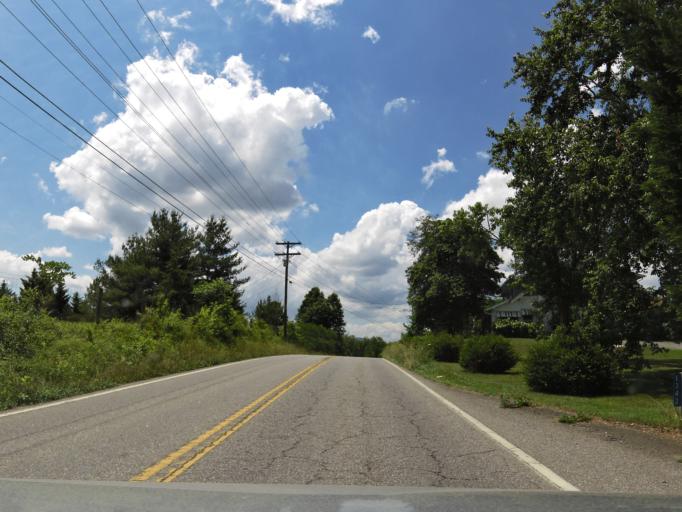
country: US
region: Tennessee
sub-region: Loudon County
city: Greenback
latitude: 35.6591
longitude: -84.0567
